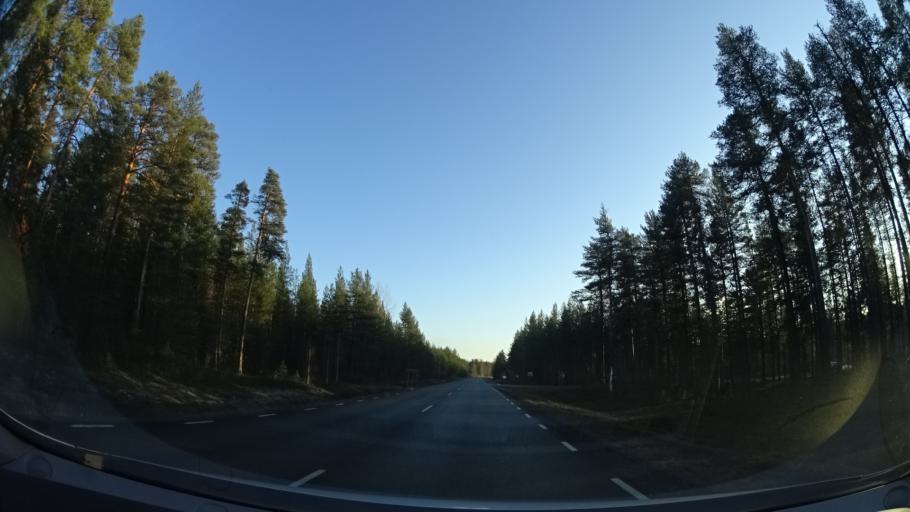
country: SE
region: Vaesterbotten
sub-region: Lycksele Kommun
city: Lycksele
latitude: 64.6147
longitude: 18.6925
